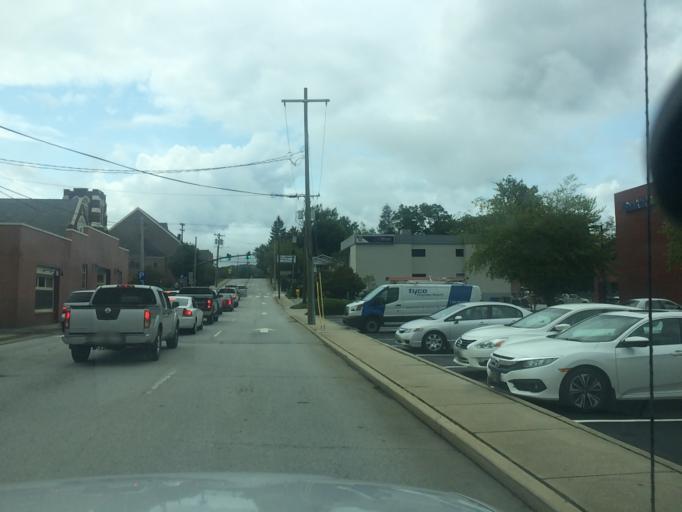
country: US
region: North Carolina
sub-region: Henderson County
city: Hendersonville
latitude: 35.3197
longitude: -82.4609
